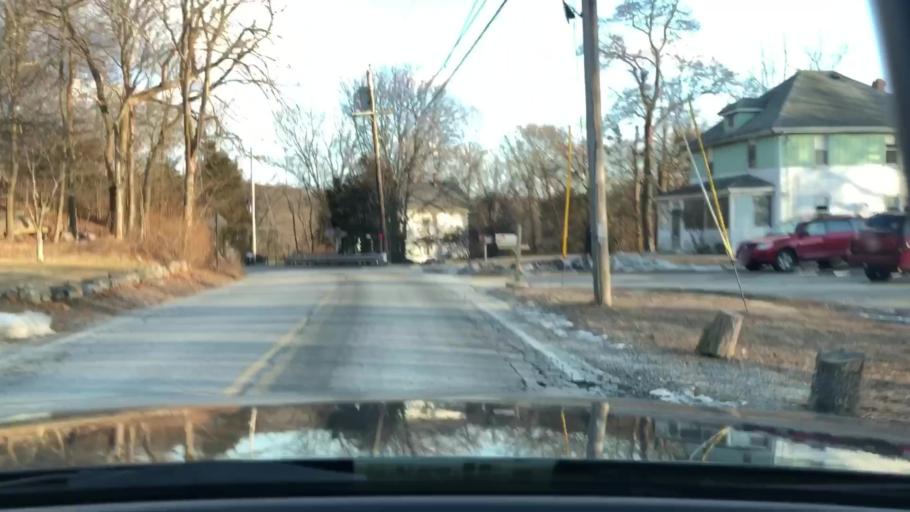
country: US
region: Massachusetts
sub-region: Worcester County
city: Millville
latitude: 42.0276
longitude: -71.5759
